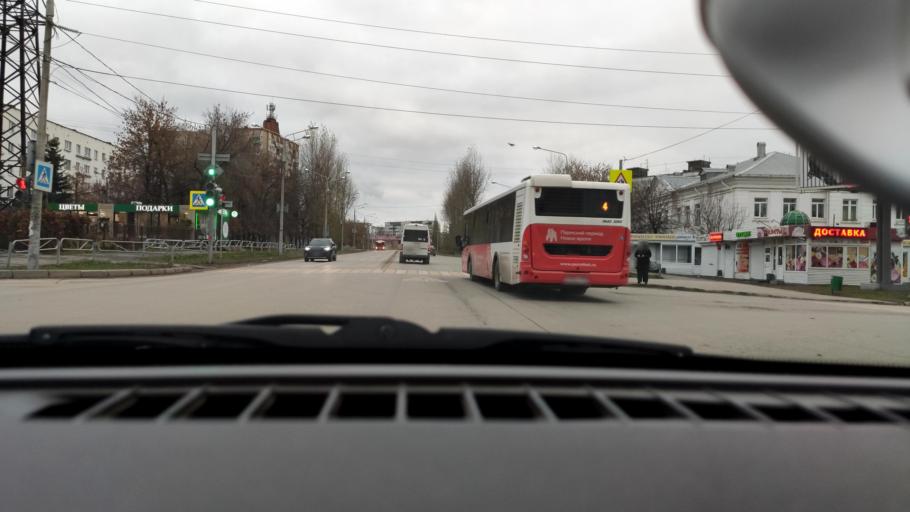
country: RU
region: Perm
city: Perm
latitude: 57.9799
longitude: 56.2166
